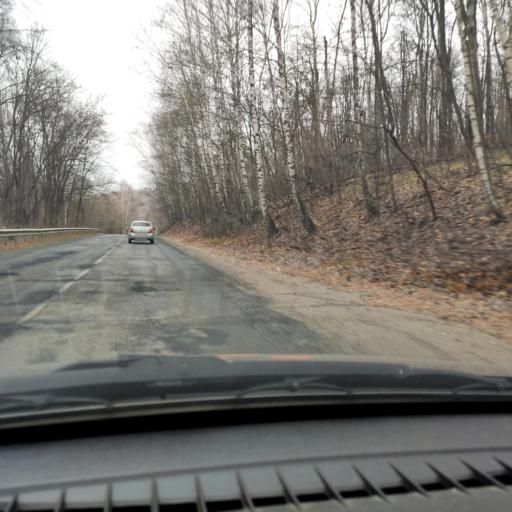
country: RU
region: Samara
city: Zhigulevsk
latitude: 53.4267
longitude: 49.6603
